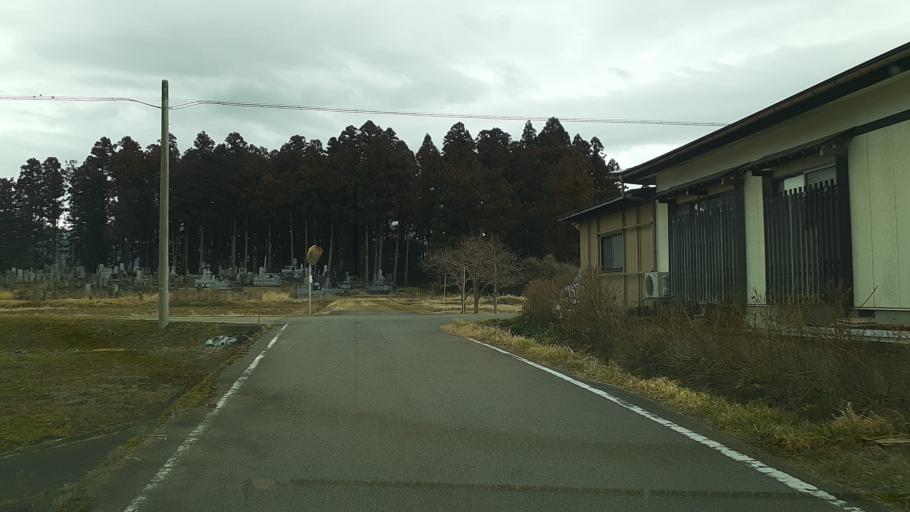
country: JP
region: Fukushima
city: Kitakata
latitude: 37.5436
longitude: 139.9137
